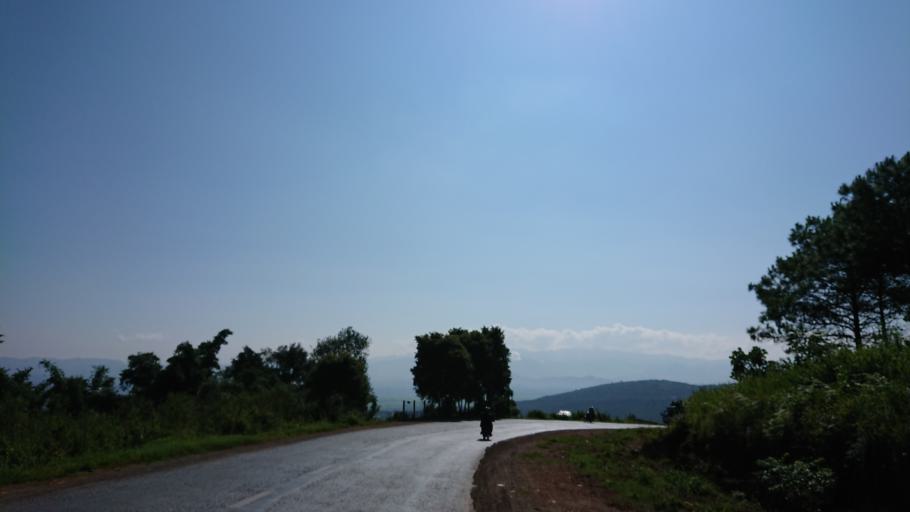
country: MM
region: Shan
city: Taunggyi
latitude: 20.7468
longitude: 97.0904
